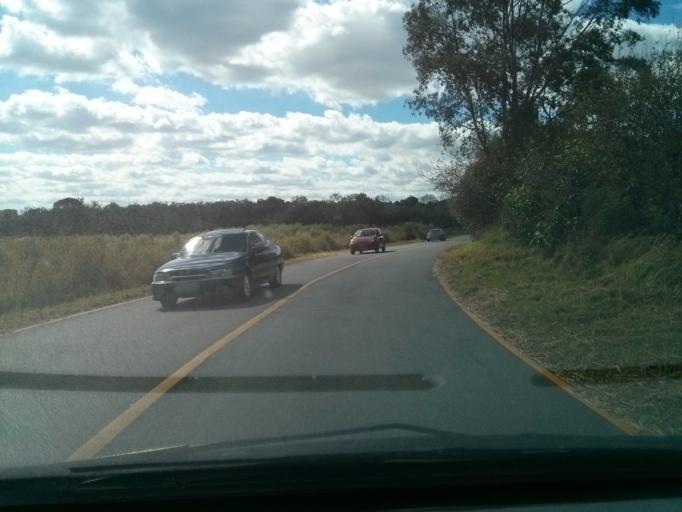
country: BR
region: Parana
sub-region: Sao Jose Dos Pinhais
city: Sao Jose dos Pinhais
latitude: -25.5435
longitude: -49.2258
